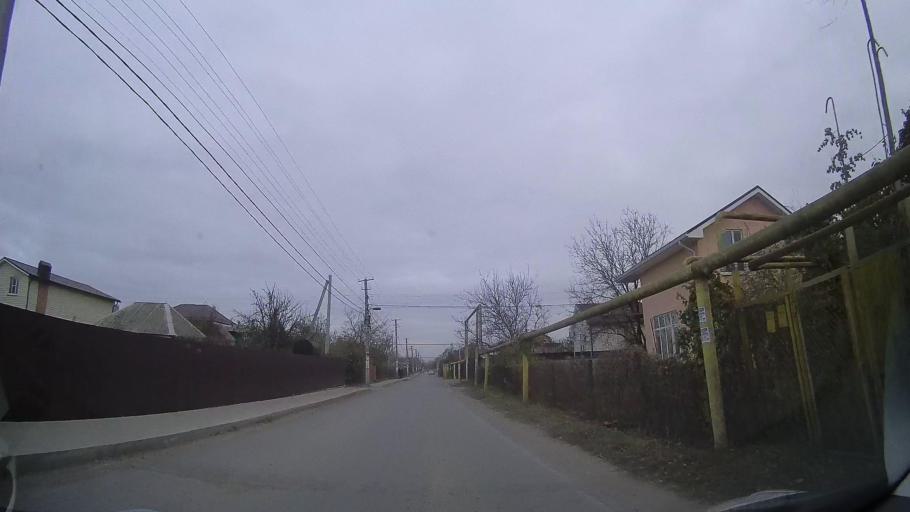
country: RU
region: Rostov
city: Bataysk
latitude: 47.0830
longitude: 39.7616
